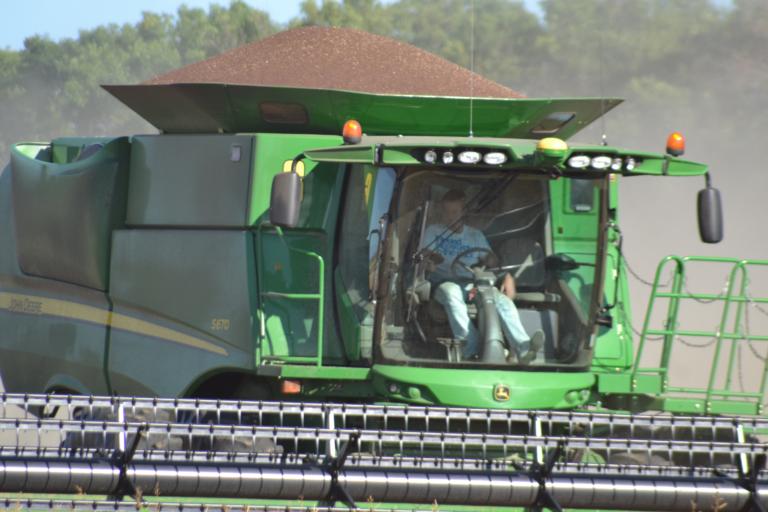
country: US
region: North Dakota
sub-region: Mercer County
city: Beulah
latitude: 47.7463
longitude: -101.9633
